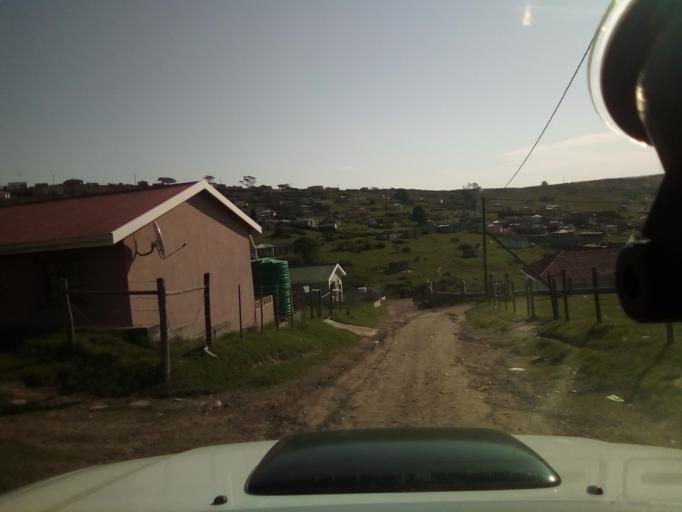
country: ZA
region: Eastern Cape
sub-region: Buffalo City Metropolitan Municipality
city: East London
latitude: -32.8453
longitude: 27.9925
